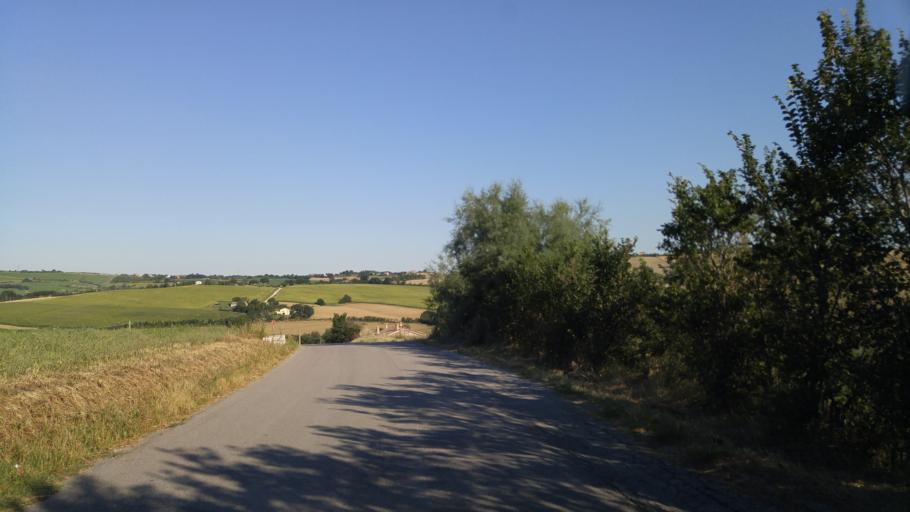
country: IT
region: The Marches
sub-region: Provincia di Pesaro e Urbino
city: Mombaroccio
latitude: 43.8124
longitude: 12.8757
